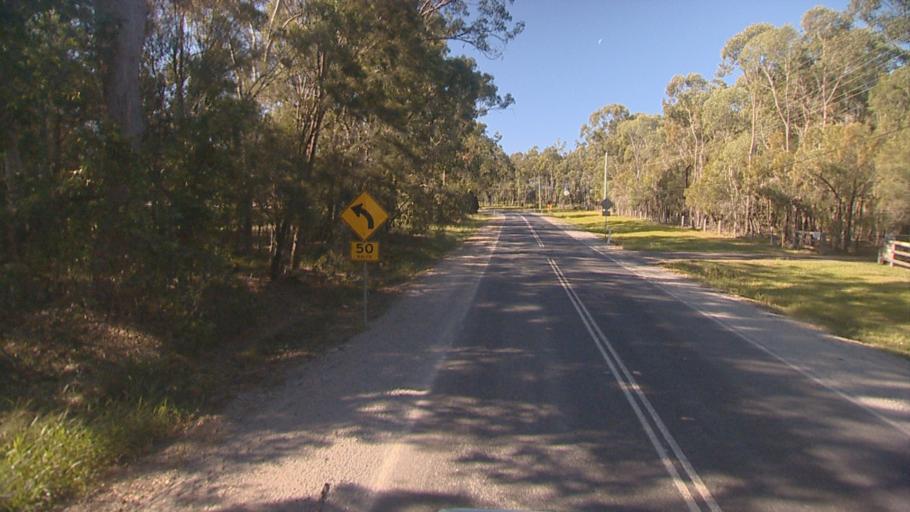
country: AU
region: Queensland
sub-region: Logan
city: Waterford West
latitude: -27.7452
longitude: 153.1413
